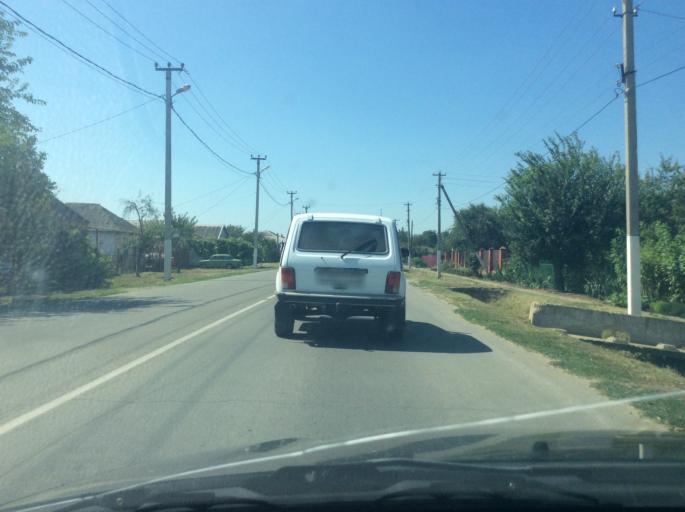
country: RU
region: Krasnodarskiy
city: Slavyansk-na-Kubani
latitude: 45.2506
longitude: 38.1087
